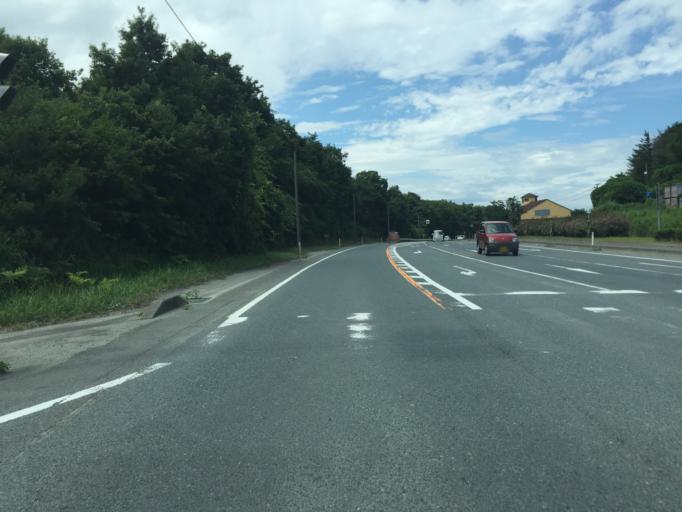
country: JP
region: Fukushima
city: Namie
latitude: 37.6687
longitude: 140.9850
